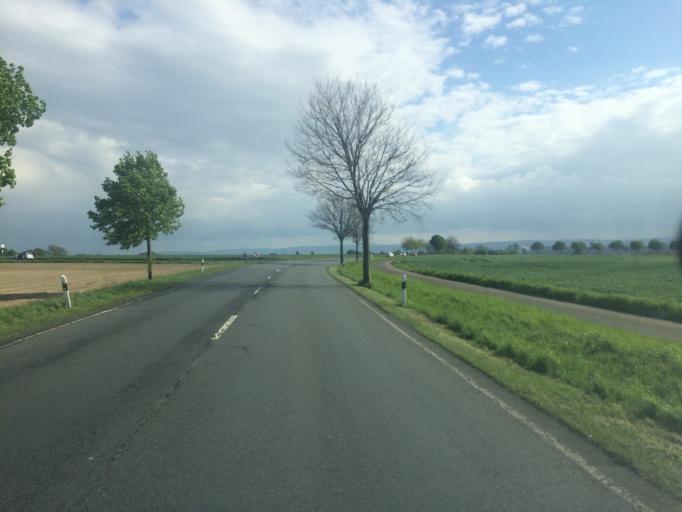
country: DE
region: Lower Saxony
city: Gross Munzel
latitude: 52.3816
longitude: 9.4803
